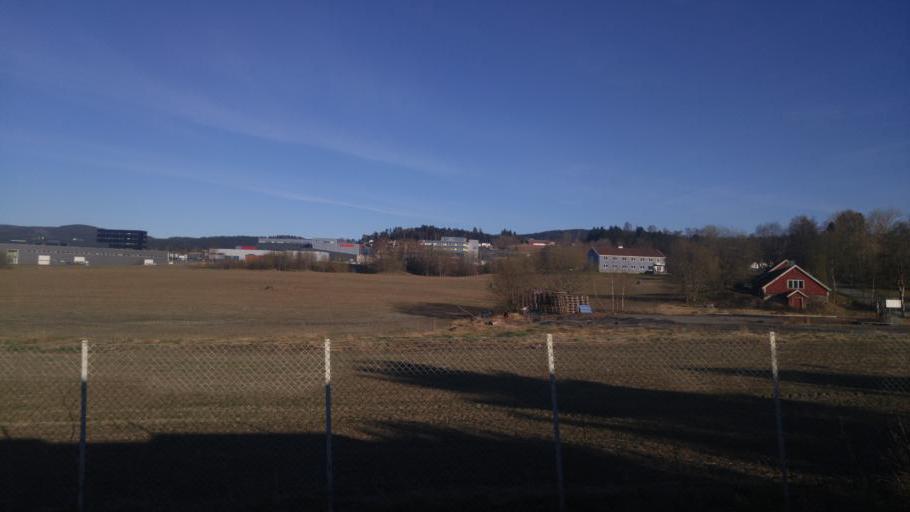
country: NO
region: Sor-Trondelag
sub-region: Trondheim
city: Trondheim
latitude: 63.4233
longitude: 10.4544
